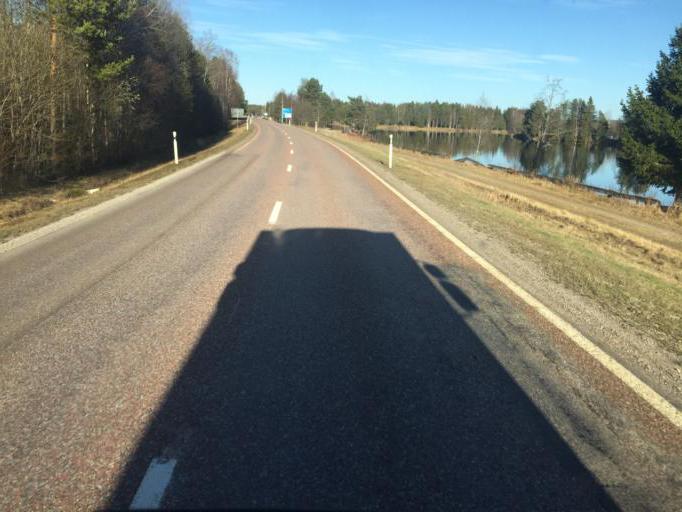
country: SE
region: Dalarna
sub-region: Gagnefs Kommun
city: Mockfjard
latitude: 60.4665
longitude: 14.6666
